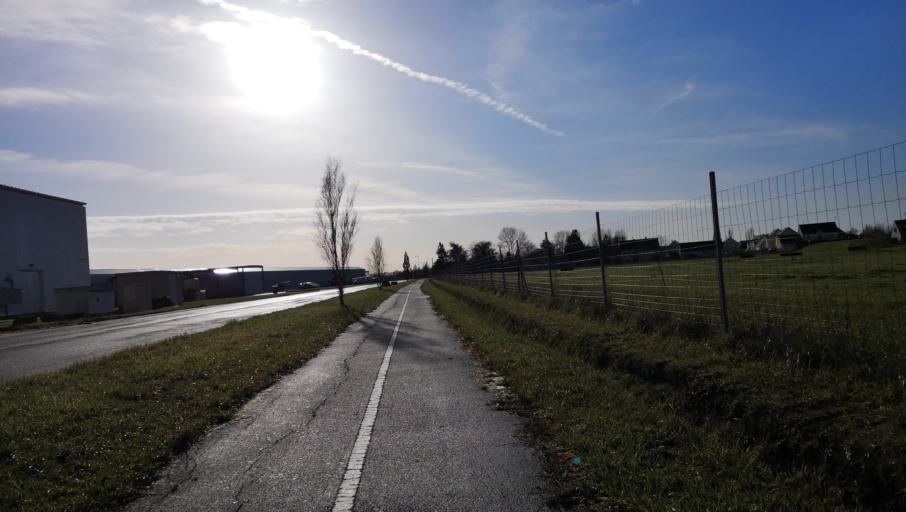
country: FR
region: Centre
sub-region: Departement du Loiret
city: Saint-Denis-en-Val
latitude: 47.8749
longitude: 1.9796
